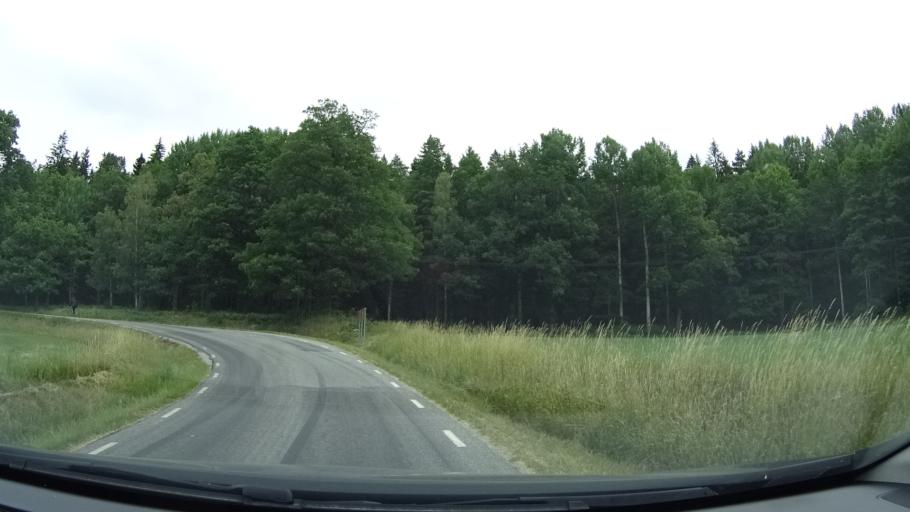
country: SE
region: Stockholm
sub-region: Varmdo Kommun
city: Mortnas
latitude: 59.3642
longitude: 18.4742
